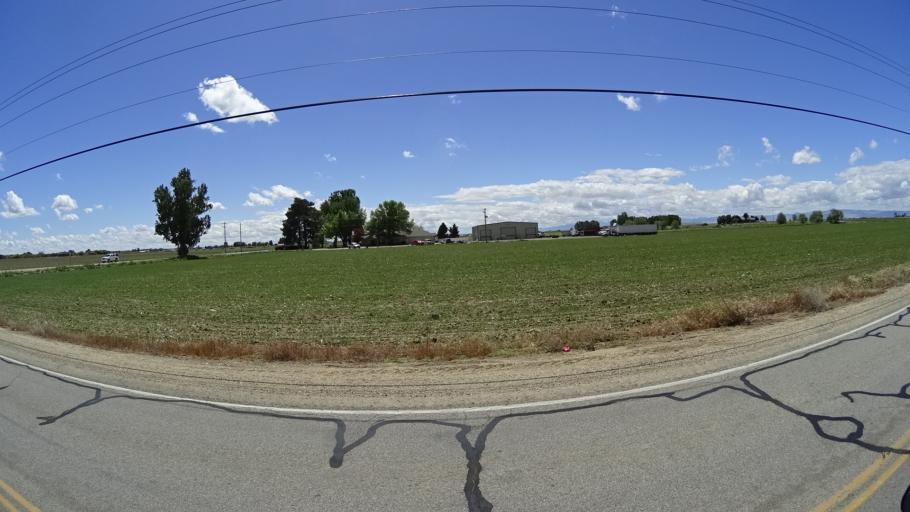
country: US
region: Idaho
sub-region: Ada County
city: Meridian
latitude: 43.5465
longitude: -116.3755
